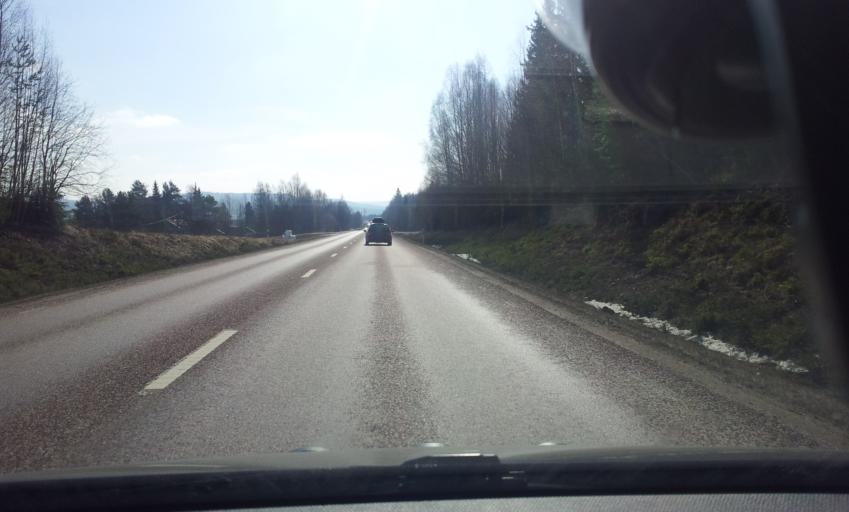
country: SE
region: Gaevleborg
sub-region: Ljusdals Kommun
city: Jaervsoe
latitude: 61.7378
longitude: 16.1604
